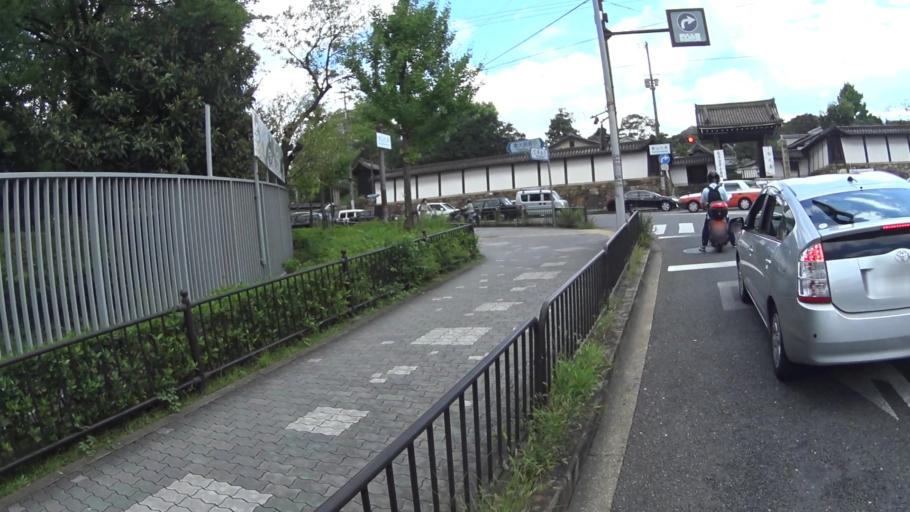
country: JP
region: Kyoto
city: Kyoto
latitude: 34.9892
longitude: 135.7740
